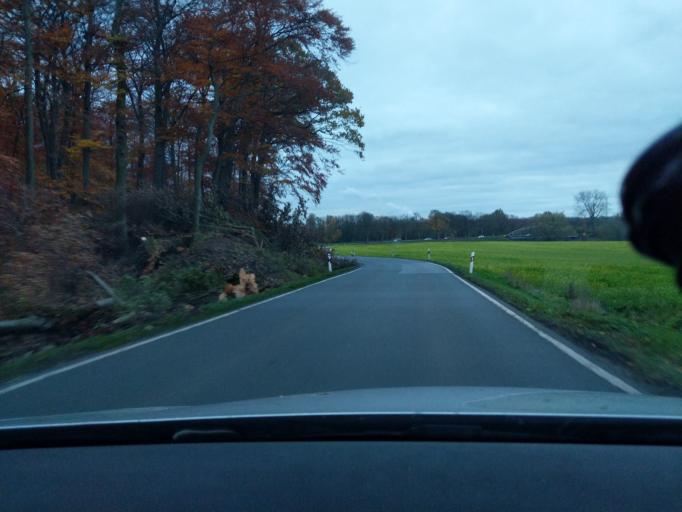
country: DE
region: North Rhine-Westphalia
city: Datteln
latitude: 51.6659
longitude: 7.4106
